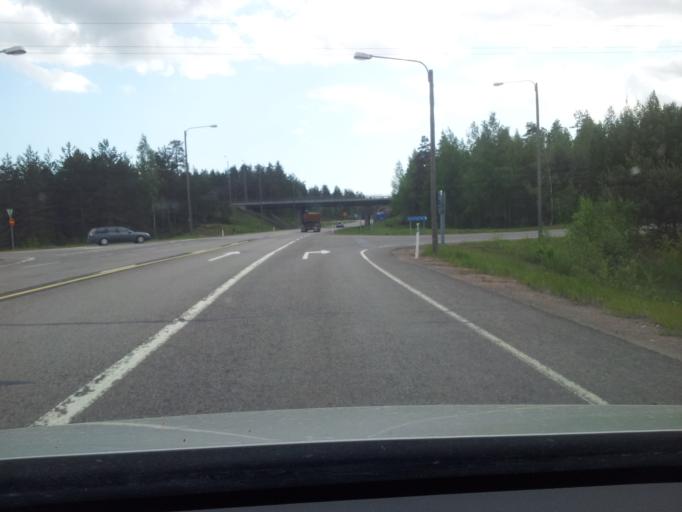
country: FI
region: South Karelia
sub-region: Lappeenranta
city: Luumaeki
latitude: 60.9300
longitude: 27.5837
